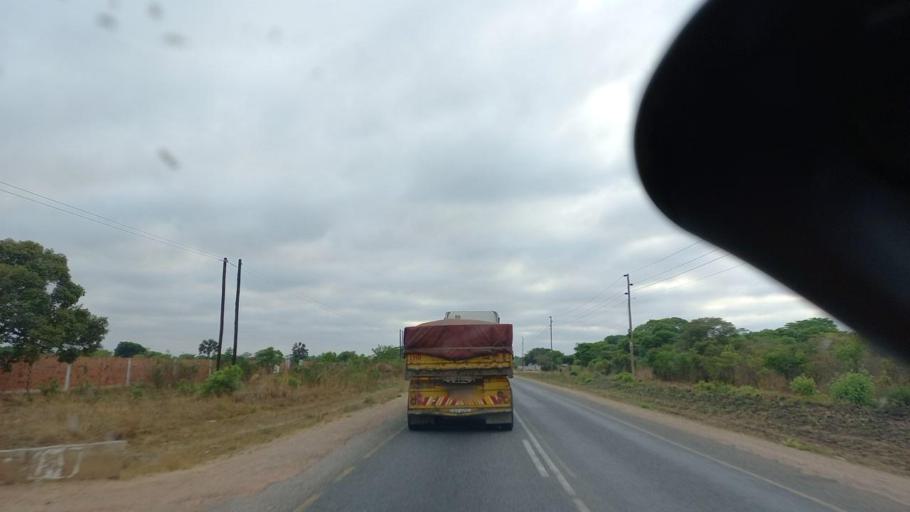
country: ZM
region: Lusaka
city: Chongwe
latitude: -15.3529
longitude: 28.5494
